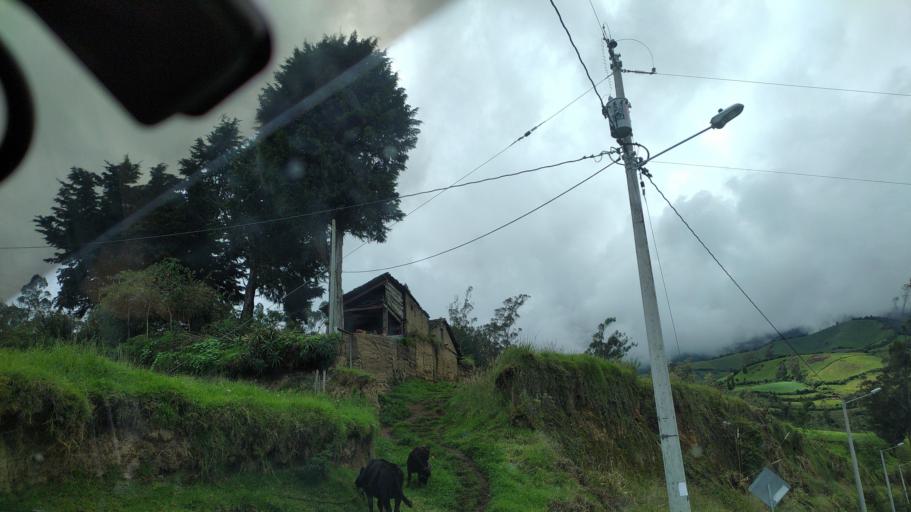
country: EC
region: Chimborazo
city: Riobamba
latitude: -1.6726
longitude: -78.5682
